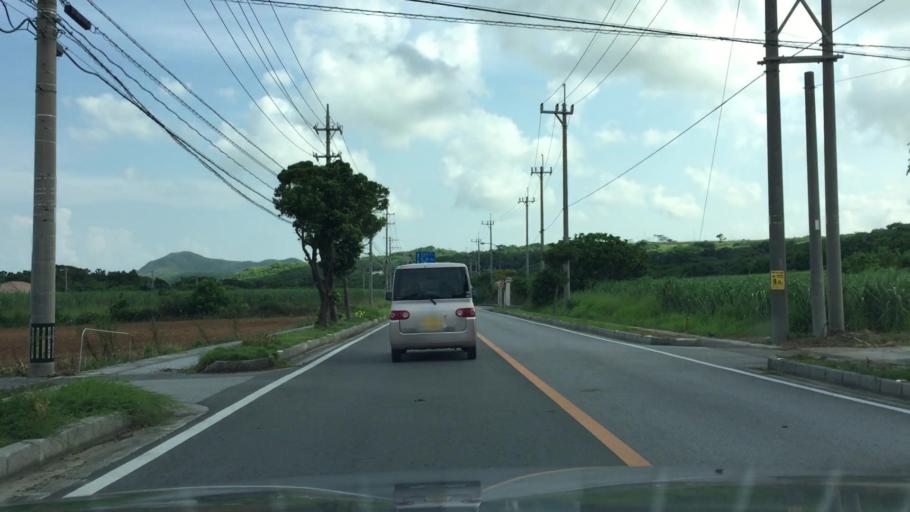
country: JP
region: Okinawa
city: Ishigaki
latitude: 24.4355
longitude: 124.2489
